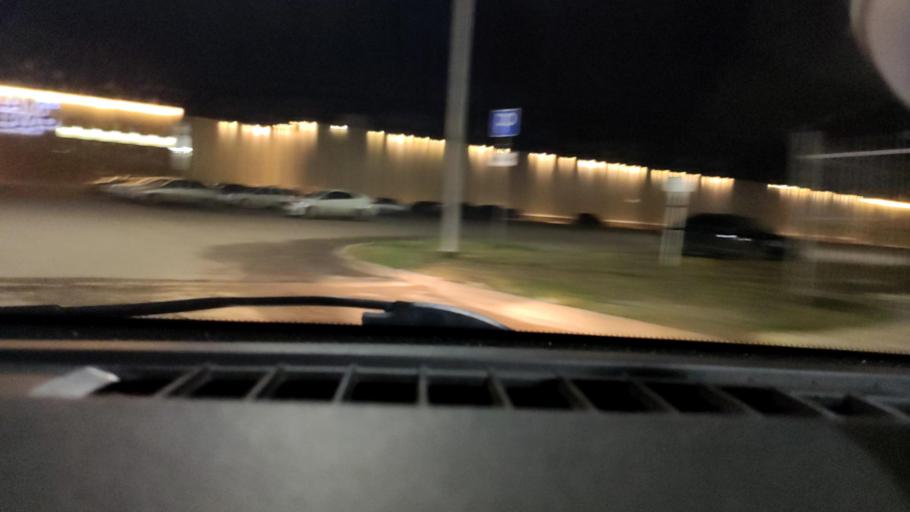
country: RU
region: Samara
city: Samara
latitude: 53.1411
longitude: 50.1714
